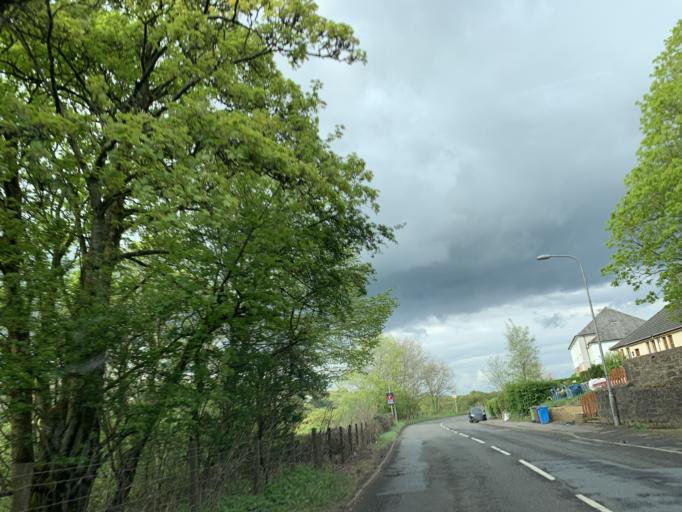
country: GB
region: Scotland
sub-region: East Renfrewshire
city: Barrhead
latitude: 55.7946
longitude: -4.4097
